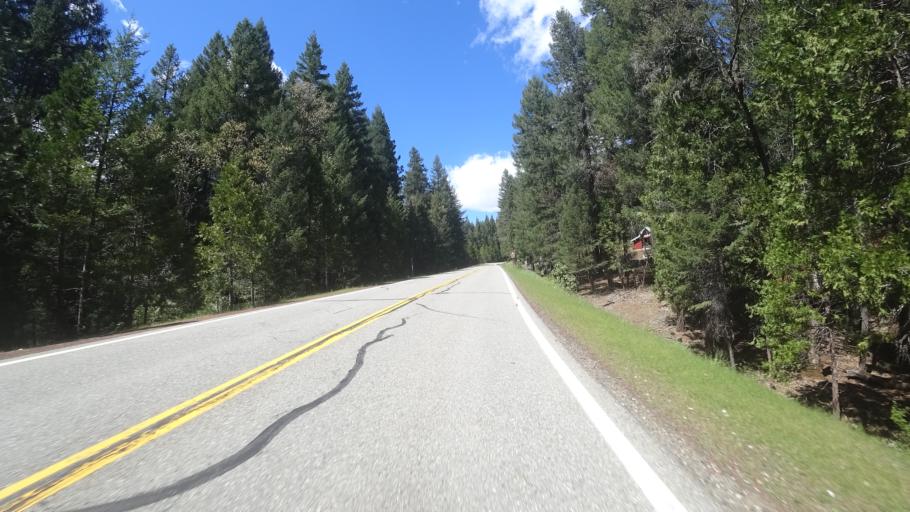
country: US
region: California
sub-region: Trinity County
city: Weaverville
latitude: 40.8102
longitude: -122.8896
